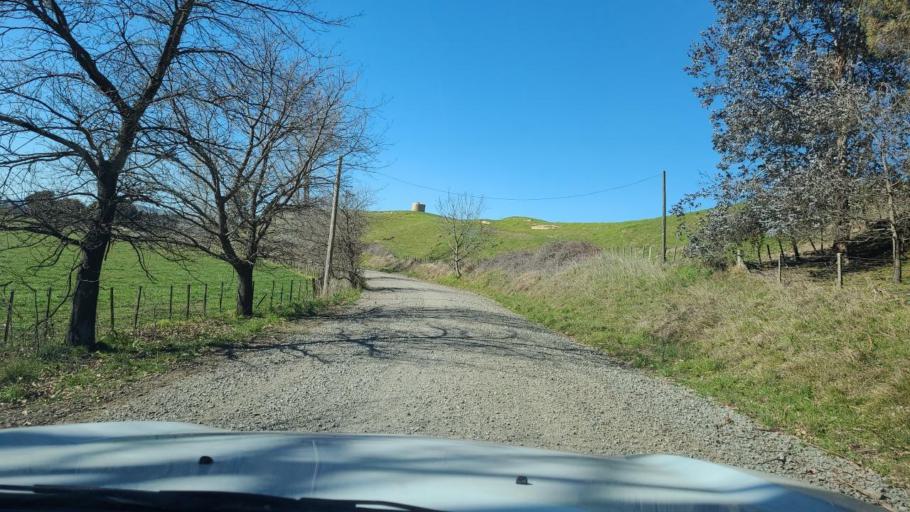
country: NZ
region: Hawke's Bay
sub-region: Napier City
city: Taradale
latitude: -39.4589
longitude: 176.5722
